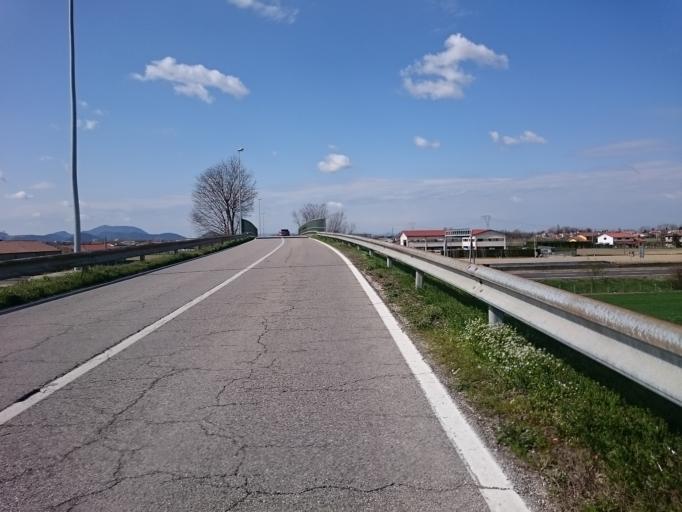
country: IT
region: Veneto
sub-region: Provincia di Padova
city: Mandriola-Sant'Agostino
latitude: 45.3528
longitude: 11.8546
